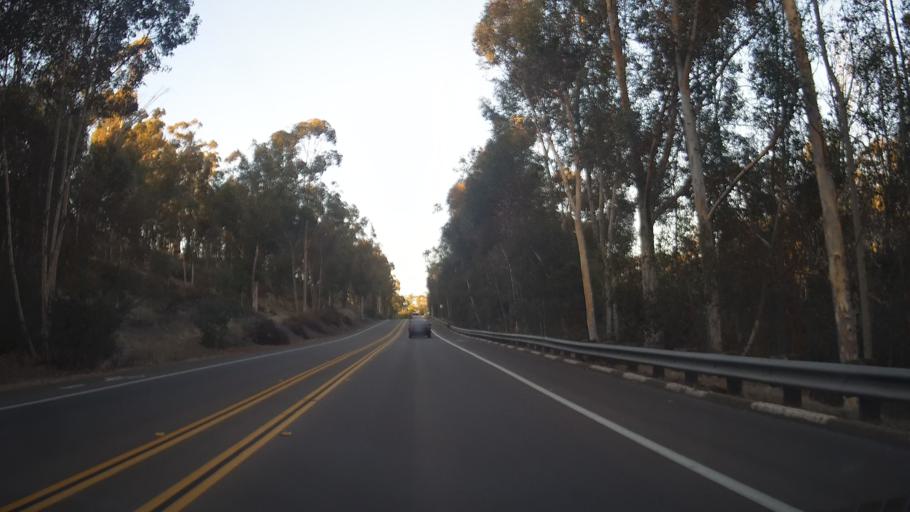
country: US
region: California
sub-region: San Diego County
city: Poway
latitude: 32.9116
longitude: -117.0735
